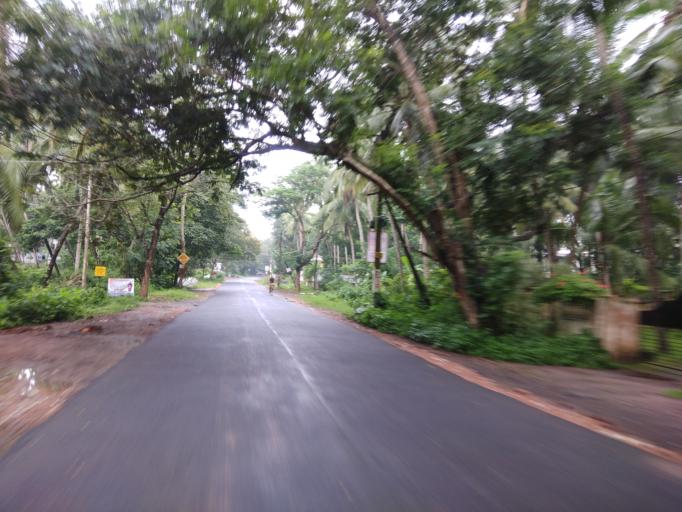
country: IN
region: Kerala
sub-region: Malappuram
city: Ponnani
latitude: 10.7598
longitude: 75.9728
